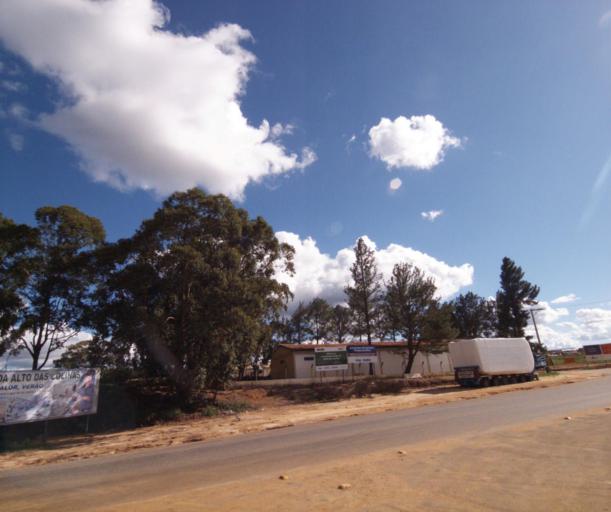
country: BR
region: Bahia
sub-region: Caetite
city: Caetite
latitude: -14.0634
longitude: -42.5220
